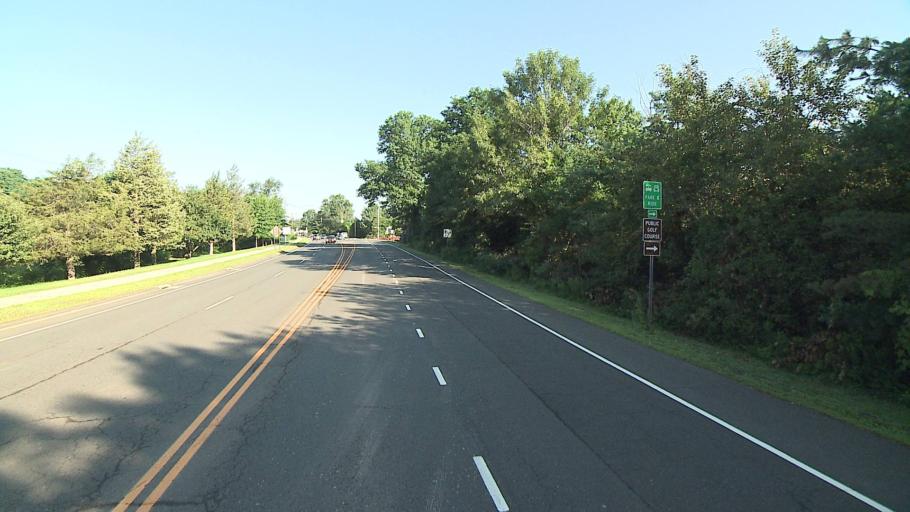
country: US
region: Connecticut
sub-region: Hartford County
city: Farmington
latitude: 41.7312
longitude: -72.8314
